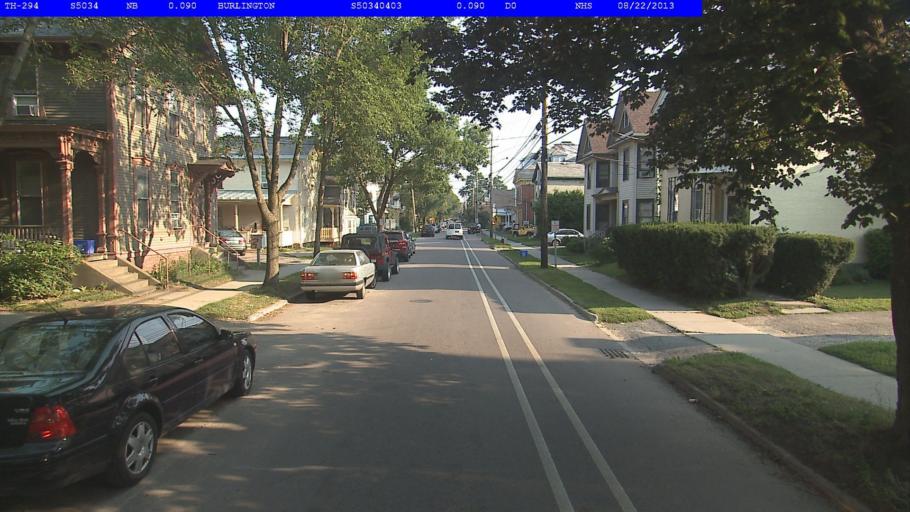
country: US
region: Vermont
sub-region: Chittenden County
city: Burlington
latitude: 44.4818
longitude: -73.2094
